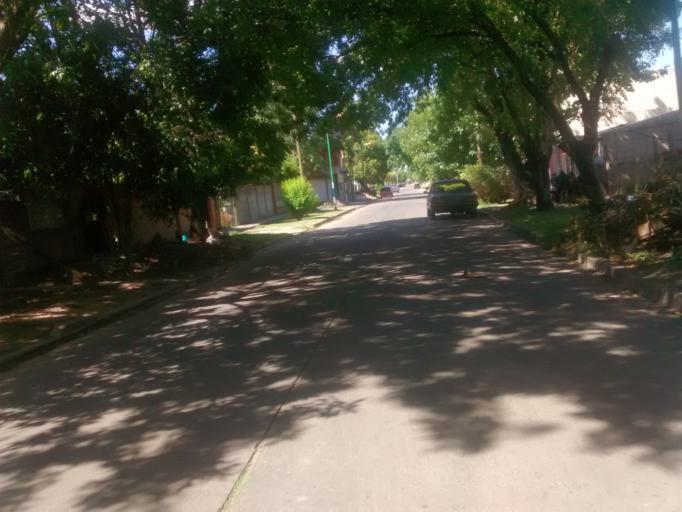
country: AR
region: Buenos Aires
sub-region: Partido de La Plata
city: La Plata
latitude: -34.9341
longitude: -57.9137
